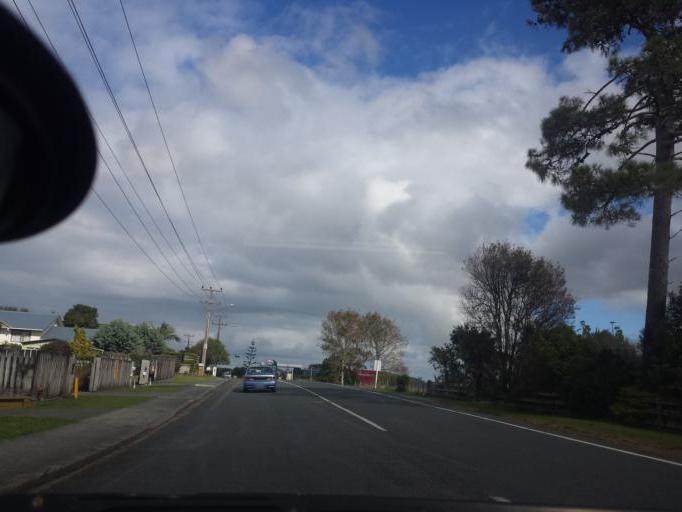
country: NZ
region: Auckland
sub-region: Auckland
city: Warkworth
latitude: -36.4157
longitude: 174.7234
